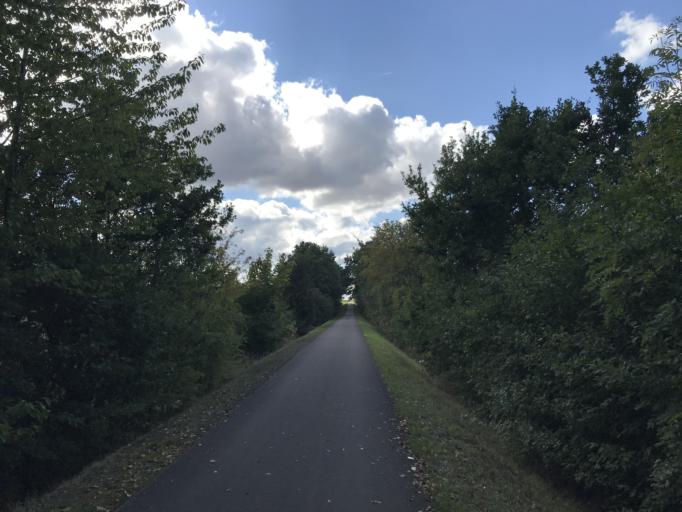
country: DE
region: Hesse
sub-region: Regierungsbezirk Kassel
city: Sachsenhausen
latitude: 51.2657
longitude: 8.9901
